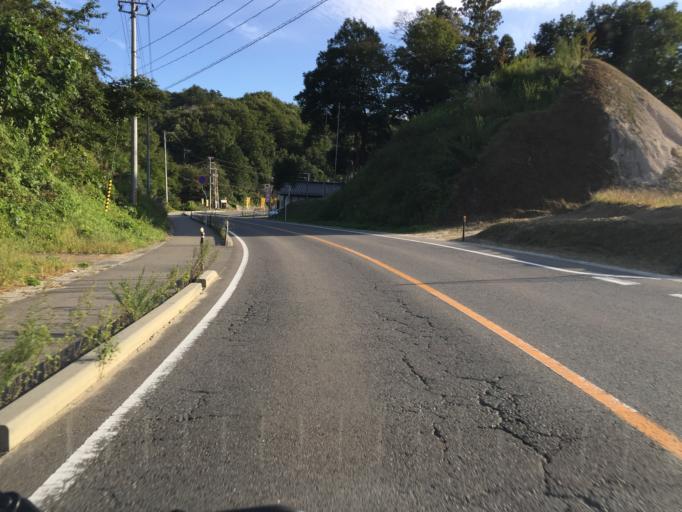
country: JP
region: Fukushima
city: Hobaramachi
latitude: 37.6794
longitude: 140.6157
